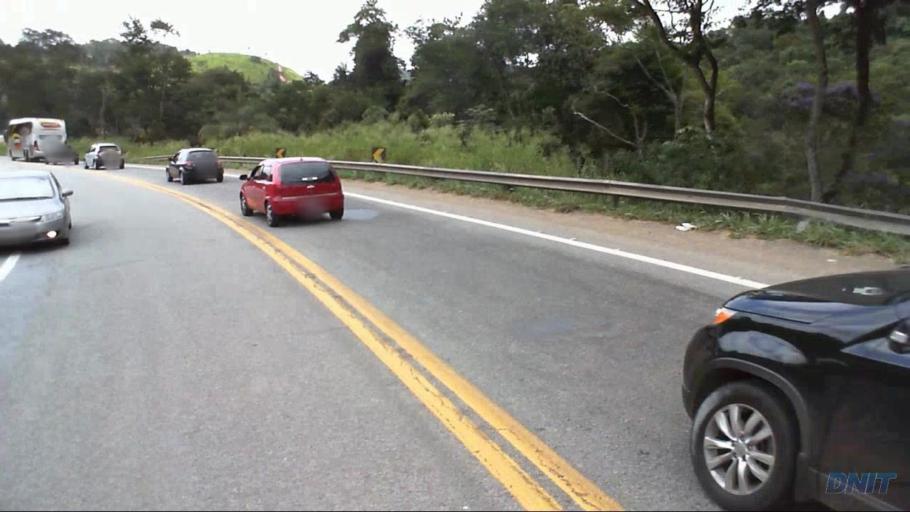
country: BR
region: Minas Gerais
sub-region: Caete
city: Caete
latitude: -19.7501
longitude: -43.6258
